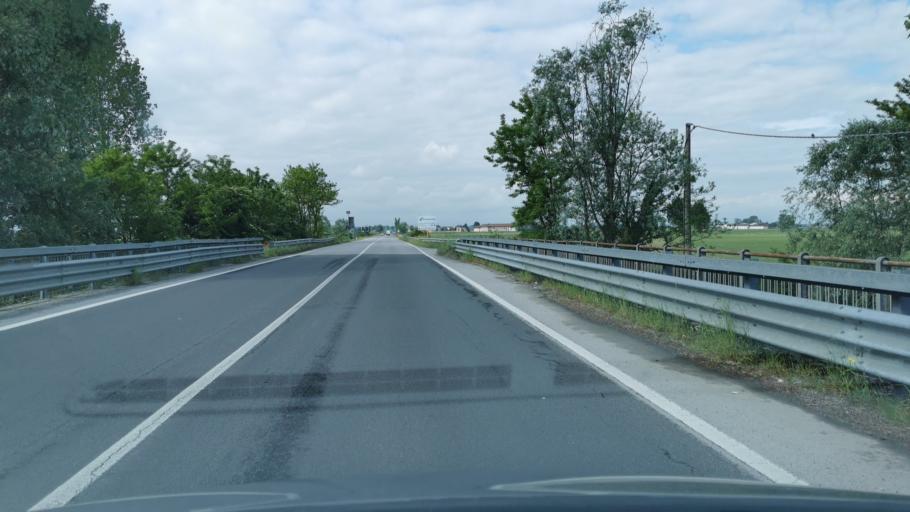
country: IT
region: Piedmont
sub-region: Provincia di Torino
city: Carmagnola
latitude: 44.8226
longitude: 7.7095
